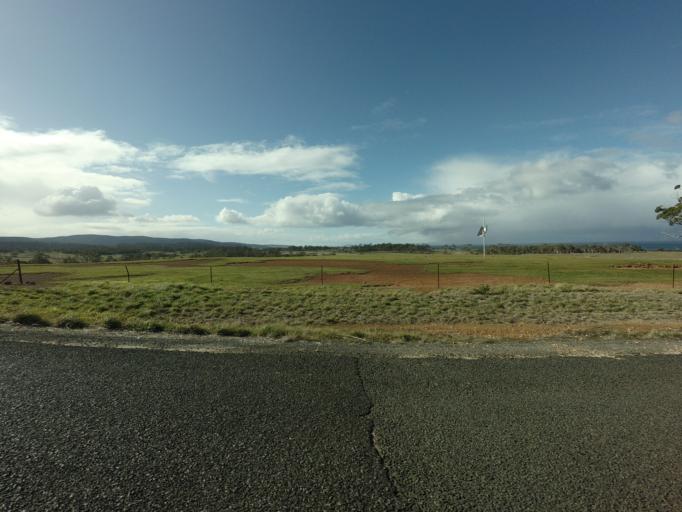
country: AU
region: Tasmania
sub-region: Sorell
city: Sorell
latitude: -42.3009
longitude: 147.9901
